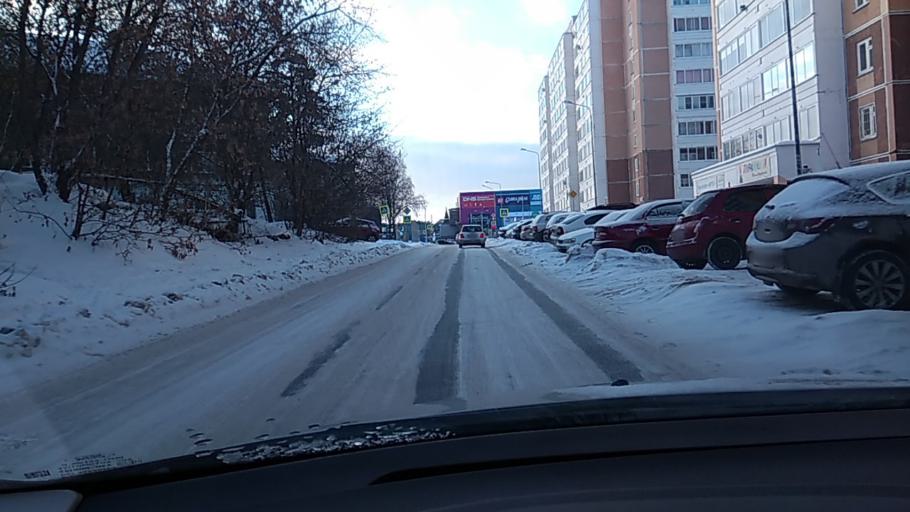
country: RU
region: Sverdlovsk
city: Sovkhoznyy
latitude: 56.8179
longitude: 60.5454
